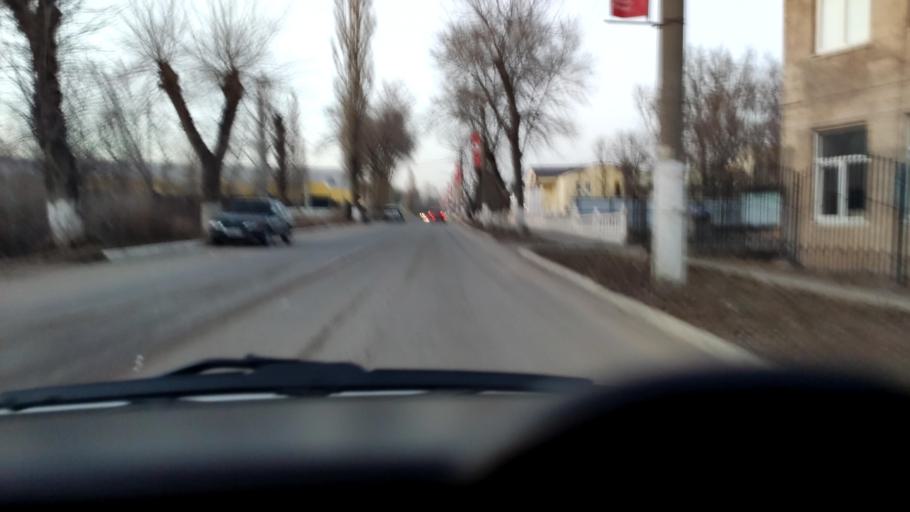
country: RU
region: Voronezj
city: Semiluki
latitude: 51.6858
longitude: 39.0400
